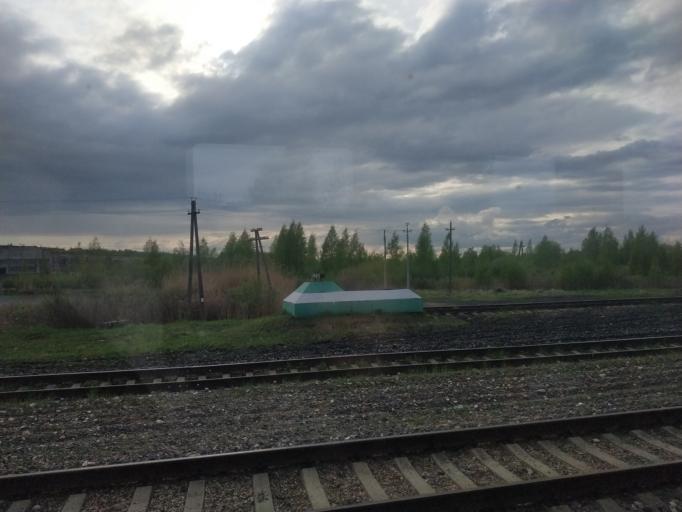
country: RU
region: Smolensk
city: Ugra
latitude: 54.7744
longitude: 34.3427
